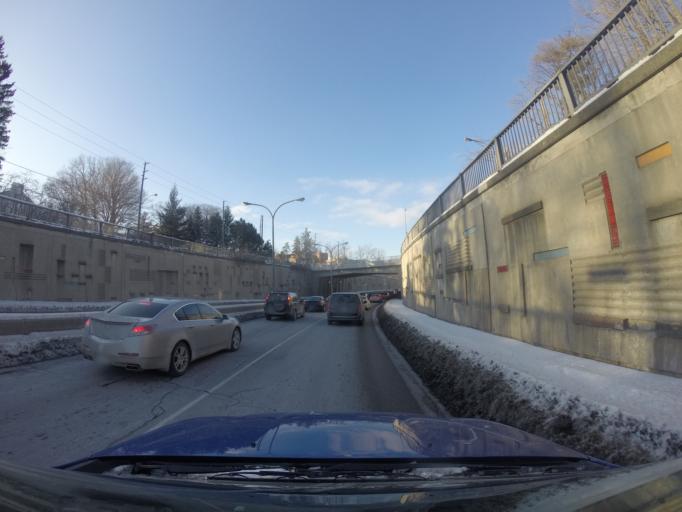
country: CA
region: Ontario
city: Willowdale
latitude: 43.7269
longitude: -79.3815
